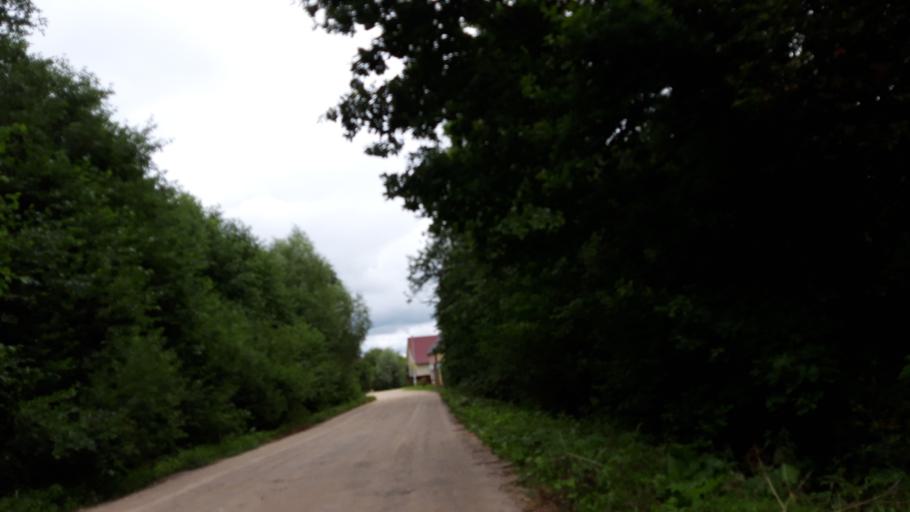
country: RU
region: Tverskaya
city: Konakovo
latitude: 56.6807
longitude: 36.7114
